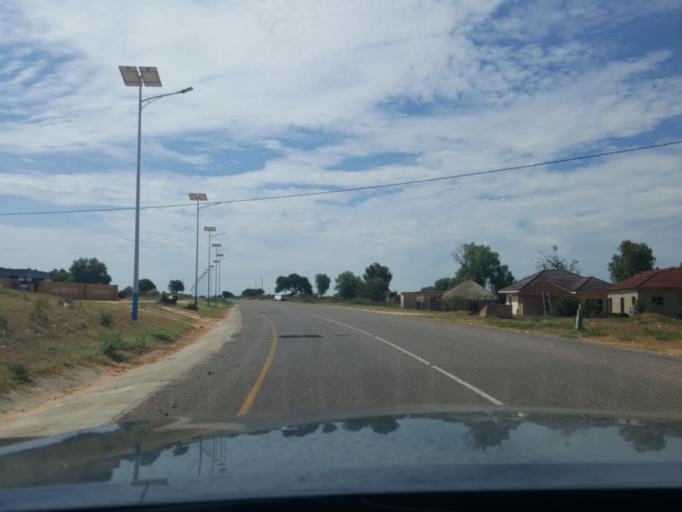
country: BW
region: Kweneng
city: Letlhakeng
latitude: -24.0841
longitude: 25.0310
